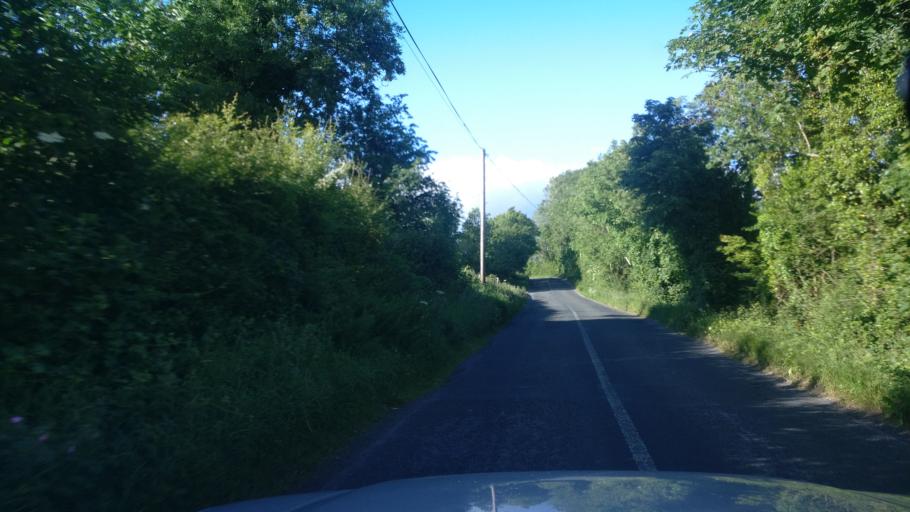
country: IE
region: Connaught
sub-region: County Galway
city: Ballinasloe
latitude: 53.2215
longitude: -8.2922
